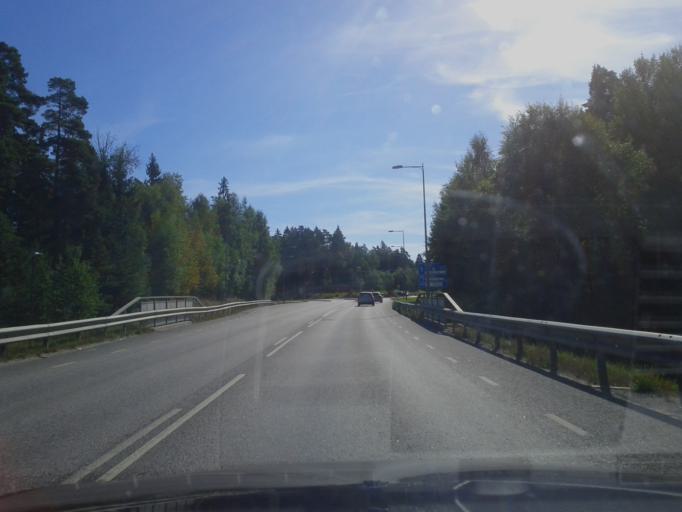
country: SE
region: Stockholm
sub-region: Taby Kommun
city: Taby
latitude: 59.4648
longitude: 18.0685
